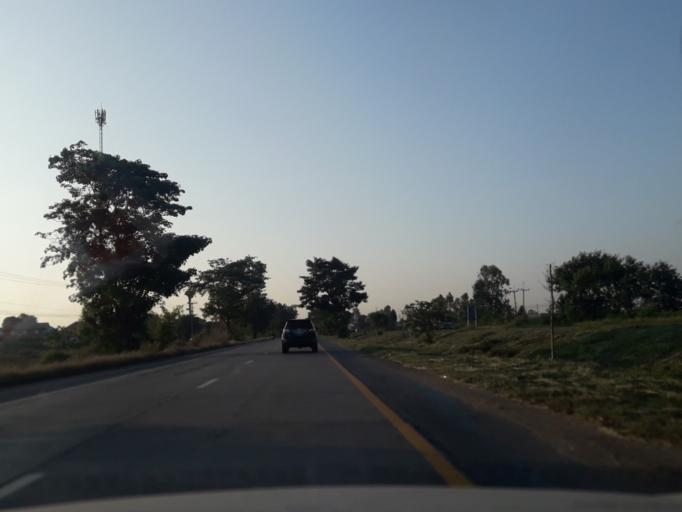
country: TH
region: Phra Nakhon Si Ayutthaya
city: Bang Pa-in
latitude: 14.2887
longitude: 100.5252
